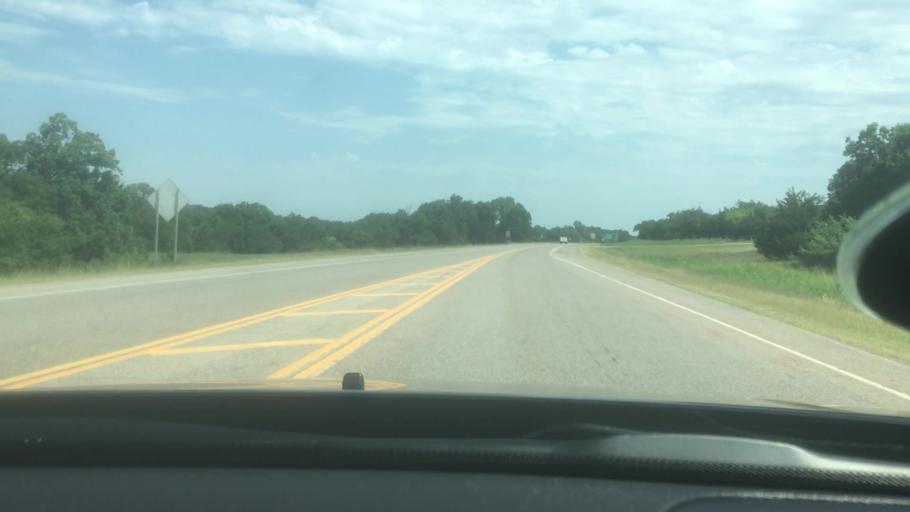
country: US
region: Oklahoma
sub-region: Seminole County
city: Konawa
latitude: 34.9887
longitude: -96.9306
